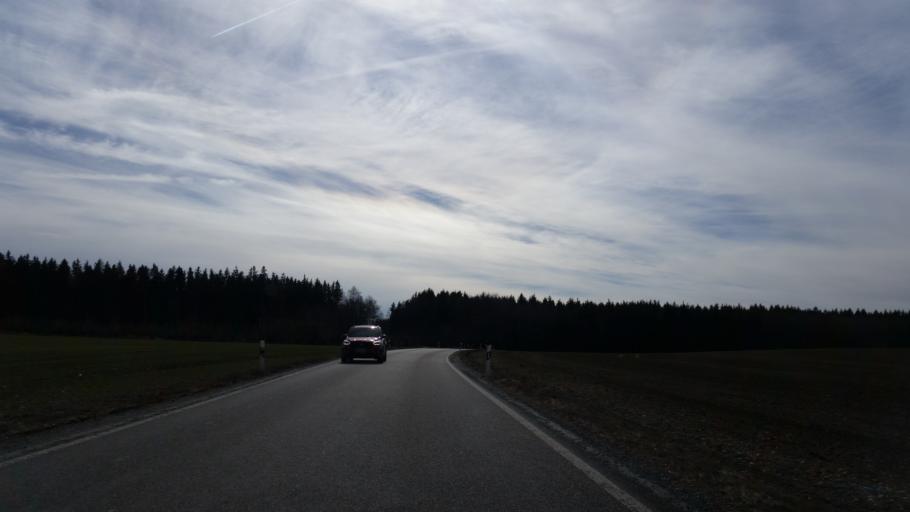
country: DE
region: Bavaria
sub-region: Upper Bavaria
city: Oberpframmern
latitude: 48.0466
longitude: 11.8159
